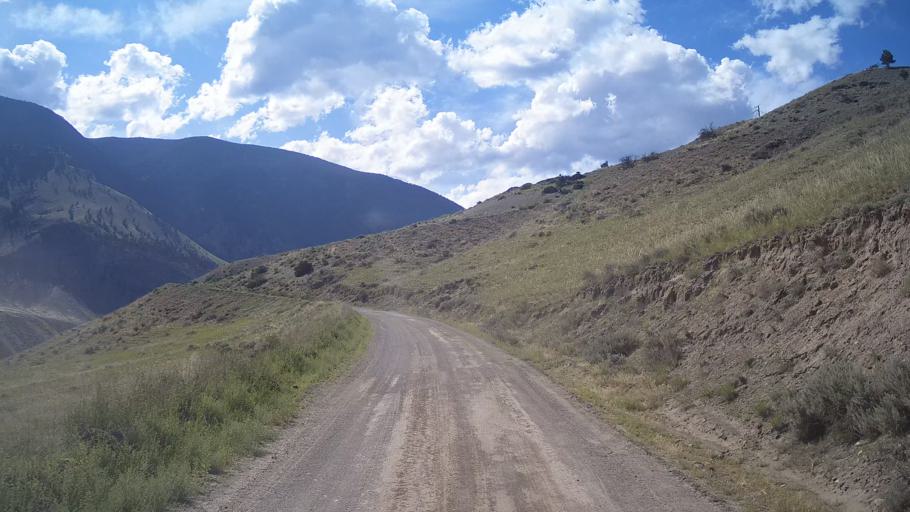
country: CA
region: British Columbia
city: Lillooet
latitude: 51.1825
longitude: -122.1164
